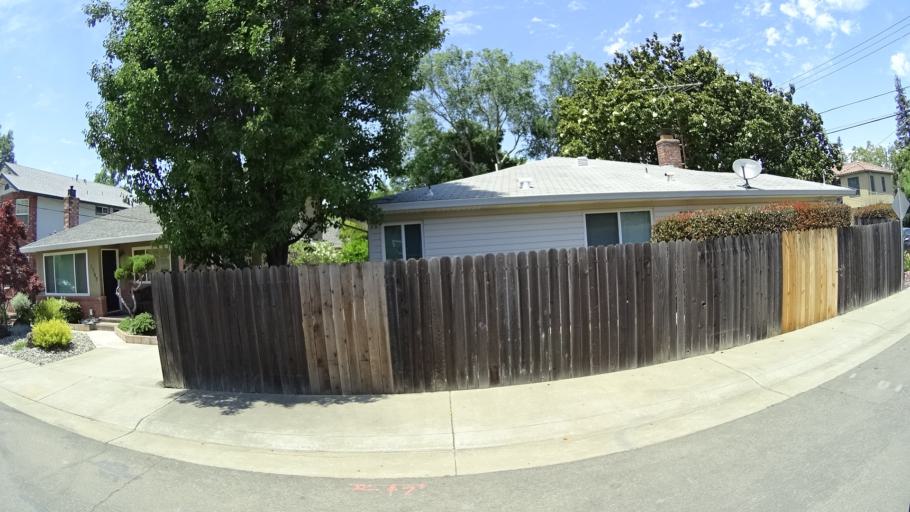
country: US
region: California
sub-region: Sacramento County
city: Sacramento
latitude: 38.5637
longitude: -121.4443
